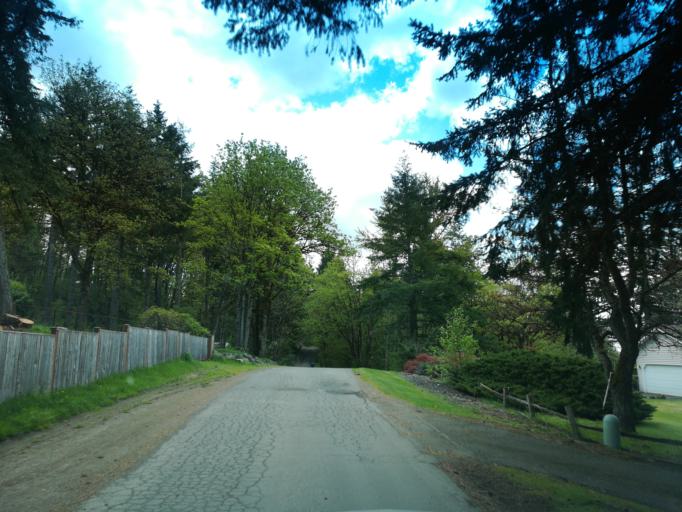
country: US
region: Oregon
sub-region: Clackamas County
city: Damascus
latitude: 45.4565
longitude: -122.4573
